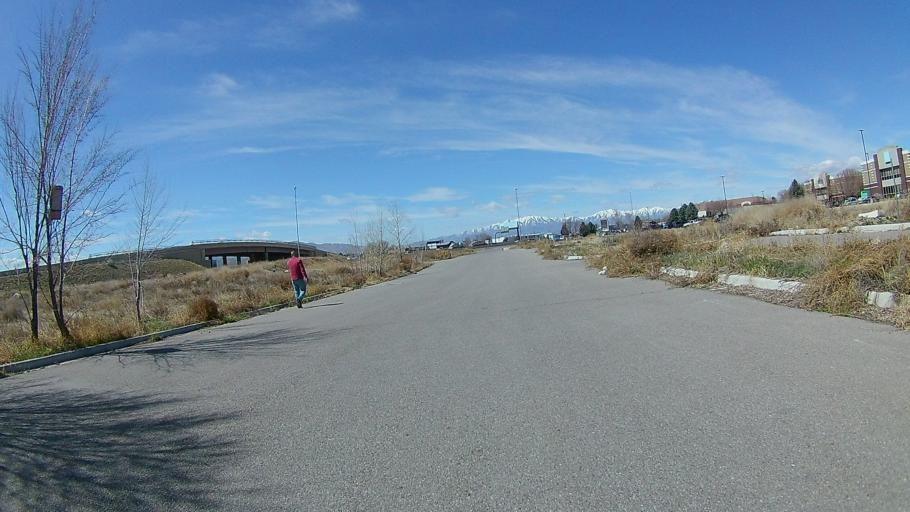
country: US
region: Utah
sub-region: Utah County
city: American Fork
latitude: 40.3563
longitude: -111.7752
